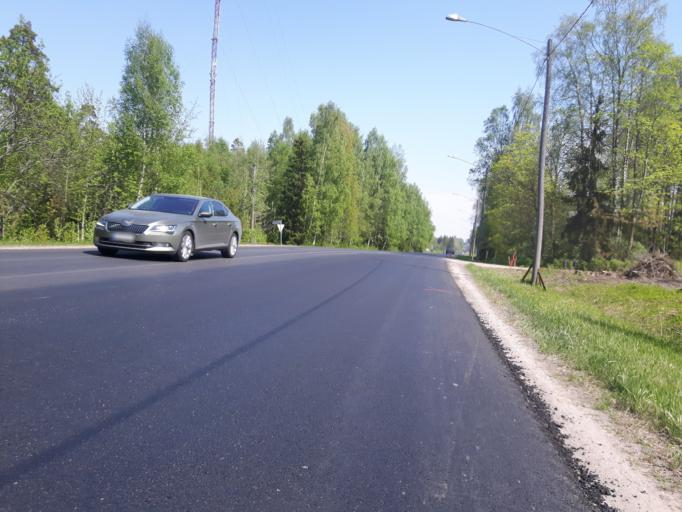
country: FI
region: Uusimaa
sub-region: Helsinki
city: Nickby
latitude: 60.3153
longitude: 25.3984
